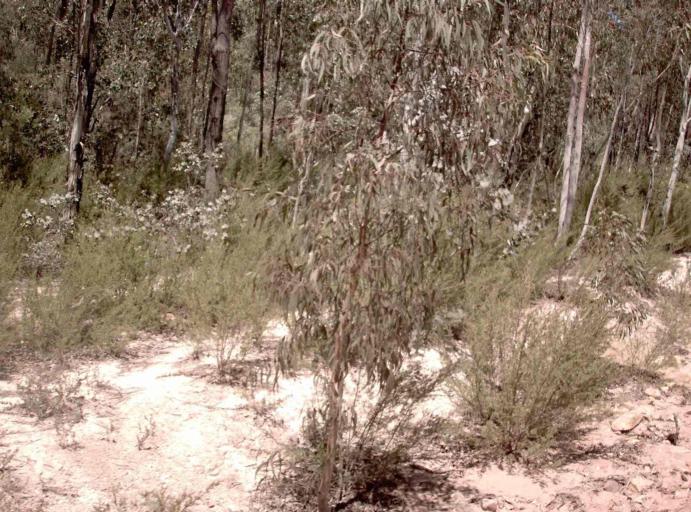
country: AU
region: New South Wales
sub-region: Snowy River
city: Jindabyne
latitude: -37.0661
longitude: 148.3187
